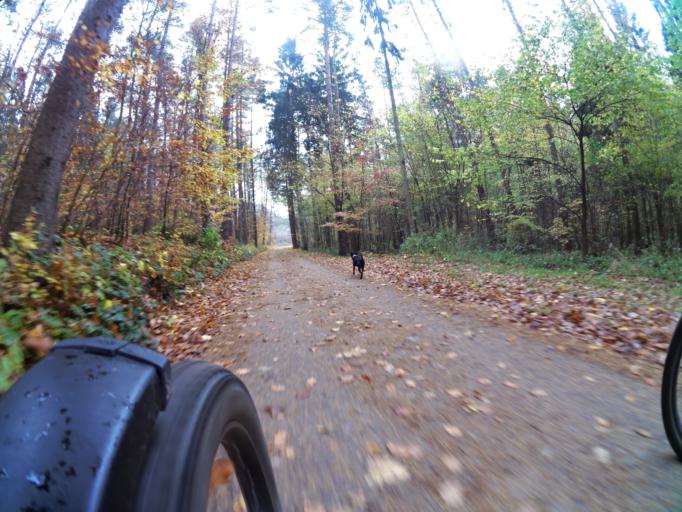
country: PL
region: Pomeranian Voivodeship
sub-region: Powiat pucki
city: Krokowa
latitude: 54.7803
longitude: 18.0904
